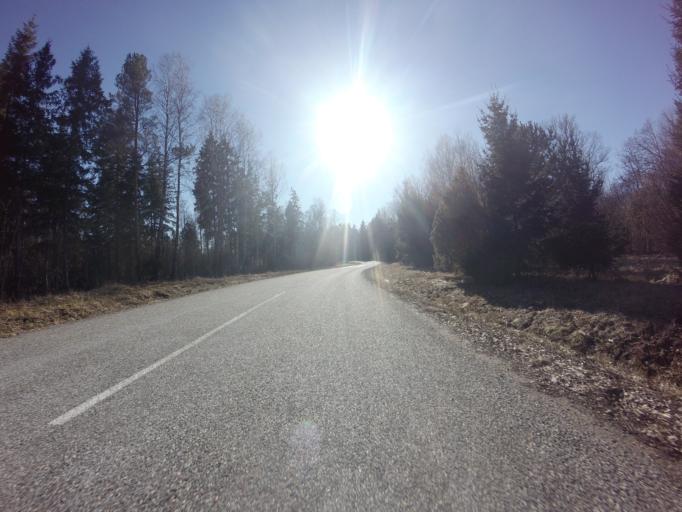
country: EE
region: Saare
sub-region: Kuressaare linn
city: Kuressaare
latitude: 58.5682
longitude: 22.4103
